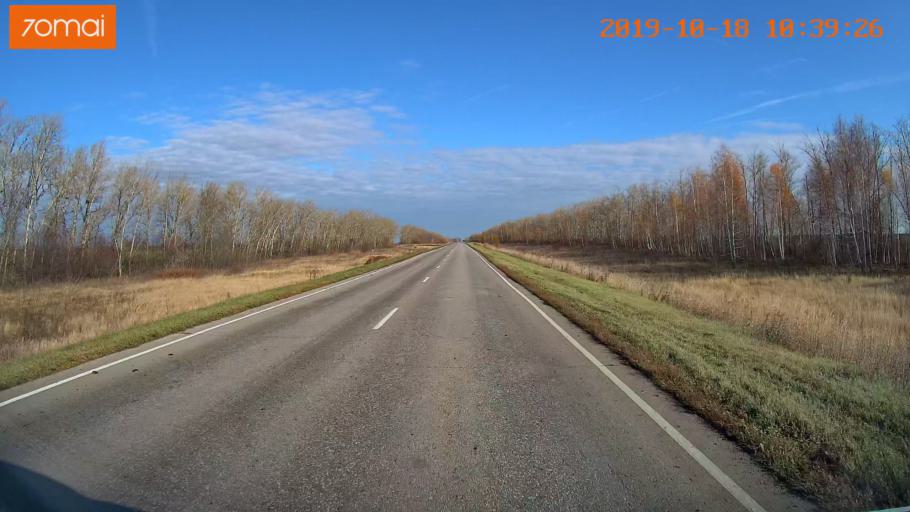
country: RU
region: Tula
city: Kurkino
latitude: 53.5868
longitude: 38.6528
